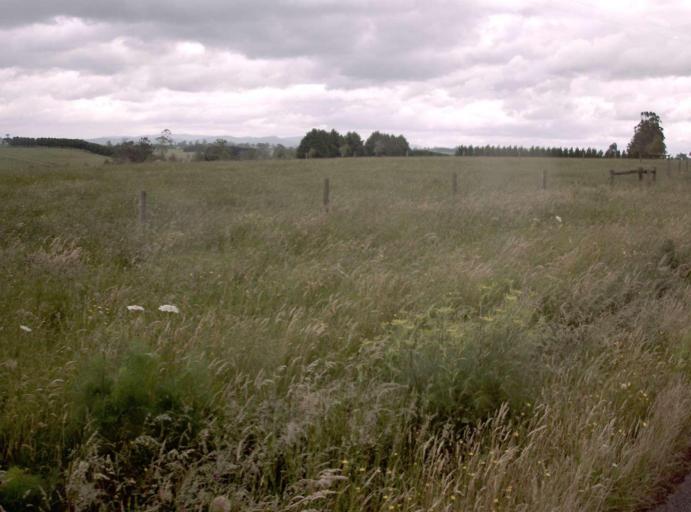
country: AU
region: Victoria
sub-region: Baw Baw
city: Warragul
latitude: -38.1496
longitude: 145.9871
